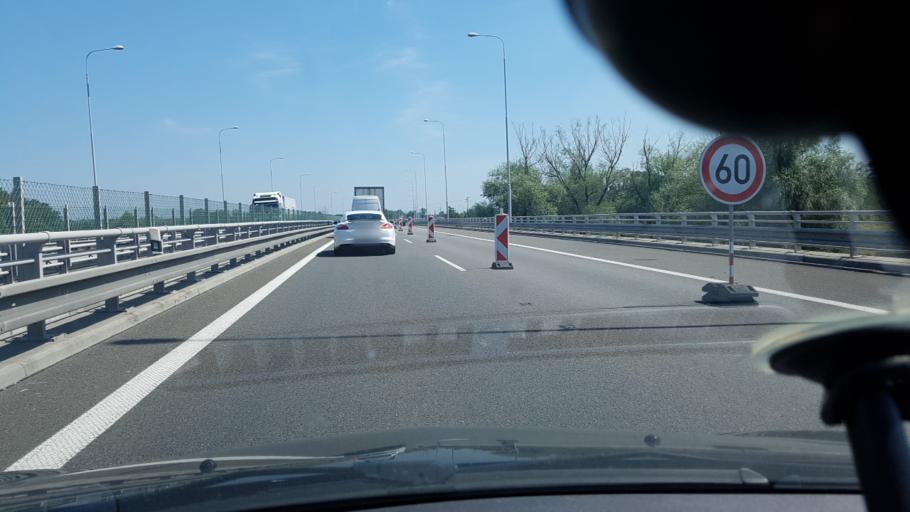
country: CZ
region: Moravskoslezsky
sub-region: Okres Ostrava-Mesto
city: Ostrava
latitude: 49.8672
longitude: 18.2789
